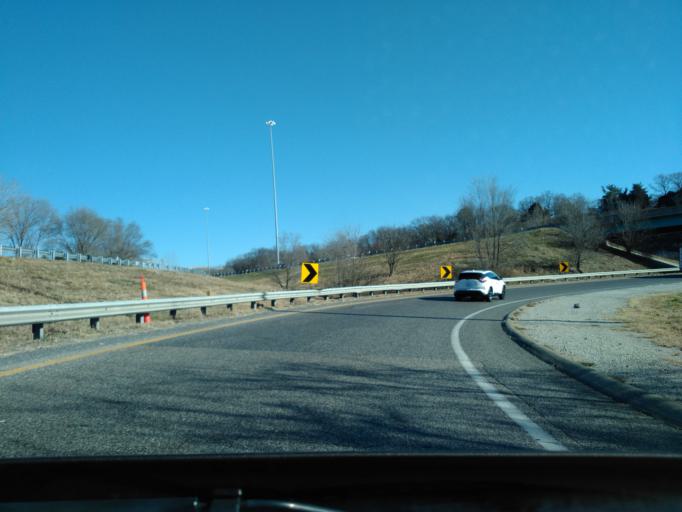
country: US
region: Missouri
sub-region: Saint Louis County
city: Sunset Hills
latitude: 38.5504
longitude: -90.4272
